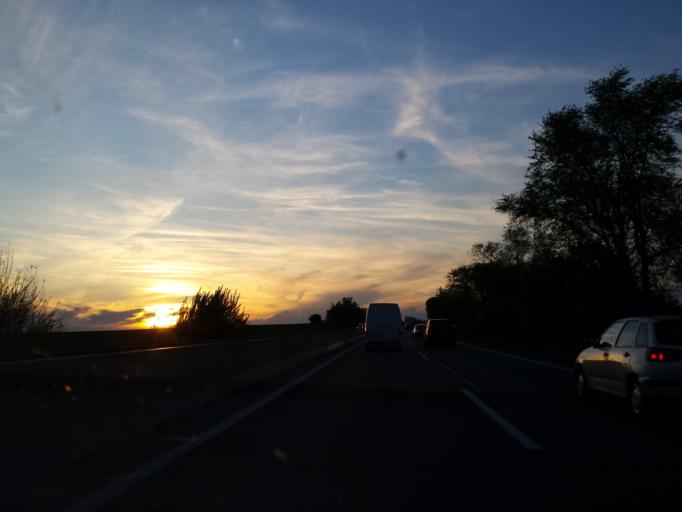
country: AT
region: Lower Austria
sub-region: Politischer Bezirk Wien-Umgebung
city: Fischamend Dorf
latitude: 48.0989
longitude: 16.6535
